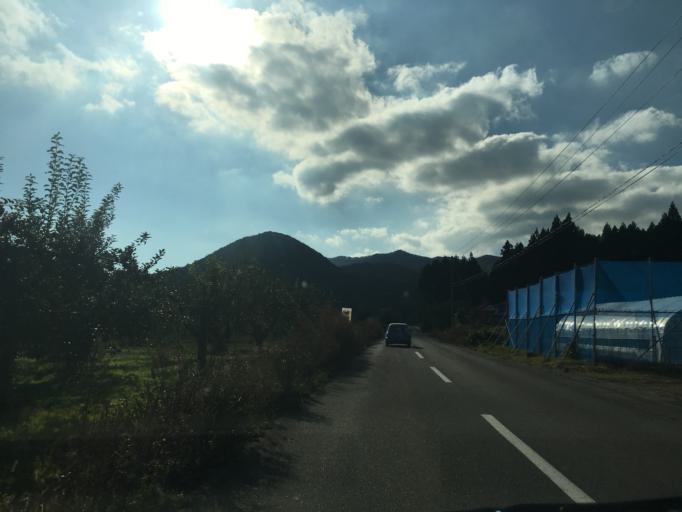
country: JP
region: Fukushima
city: Sukagawa
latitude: 37.2738
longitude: 140.1585
